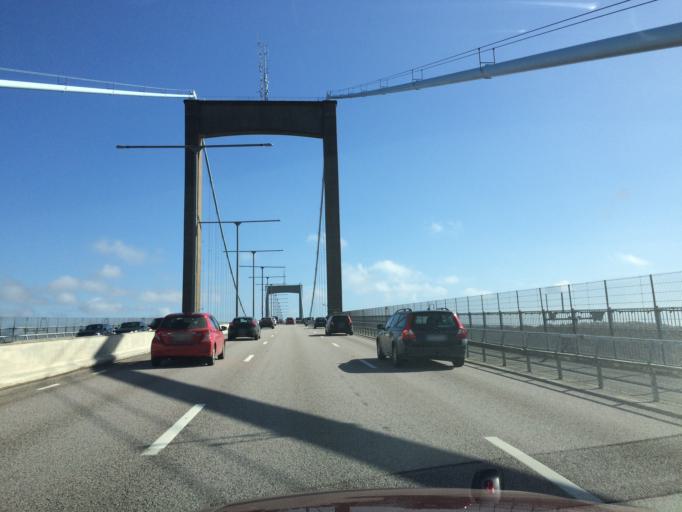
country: SE
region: Vaestra Goetaland
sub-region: Goteborg
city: Majorna
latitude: 57.6938
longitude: 11.8998
